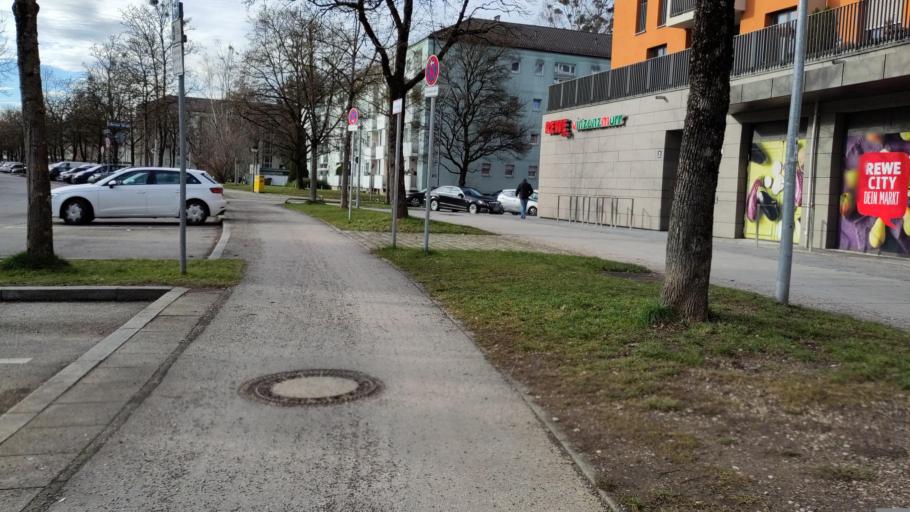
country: DE
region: Bavaria
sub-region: Upper Bavaria
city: Neuried
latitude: 48.0950
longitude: 11.4959
